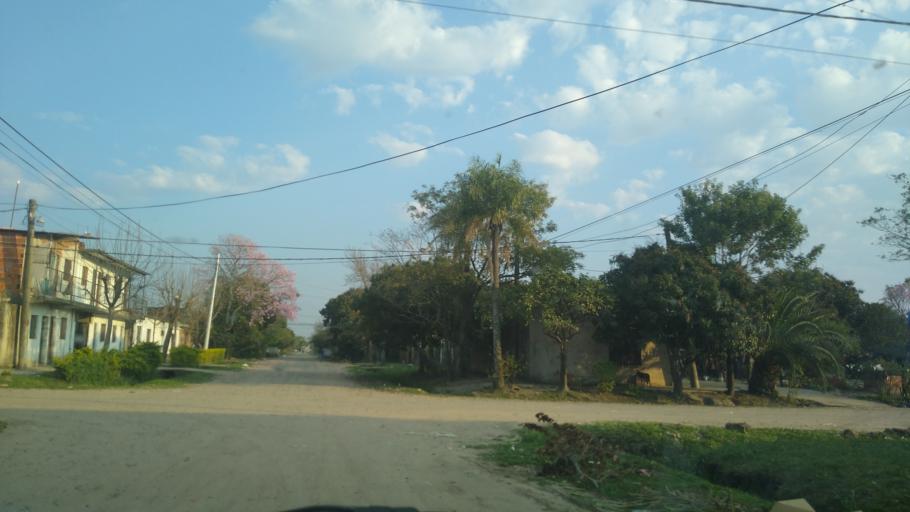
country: AR
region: Chaco
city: Resistencia
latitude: -27.4820
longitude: -58.9712
